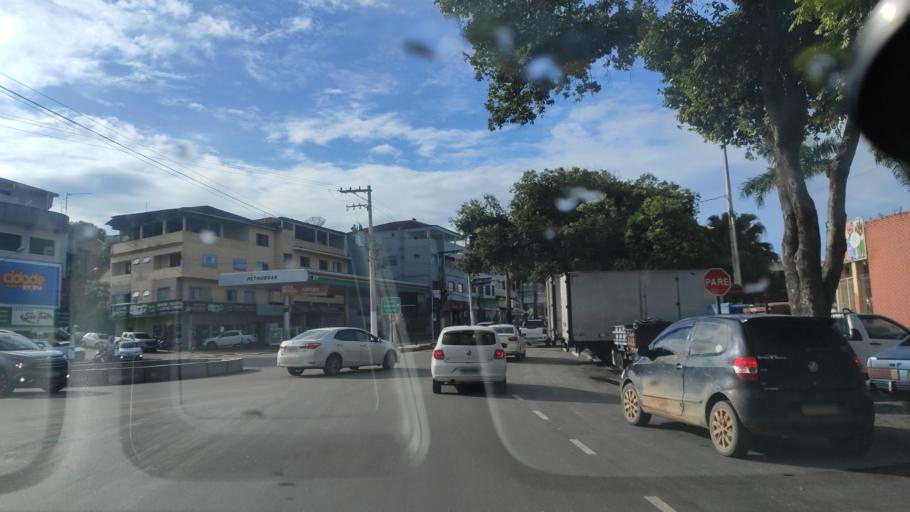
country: BR
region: Espirito Santo
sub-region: Nova Venecia
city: Nova Venecia
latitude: -18.7082
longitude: -40.3995
